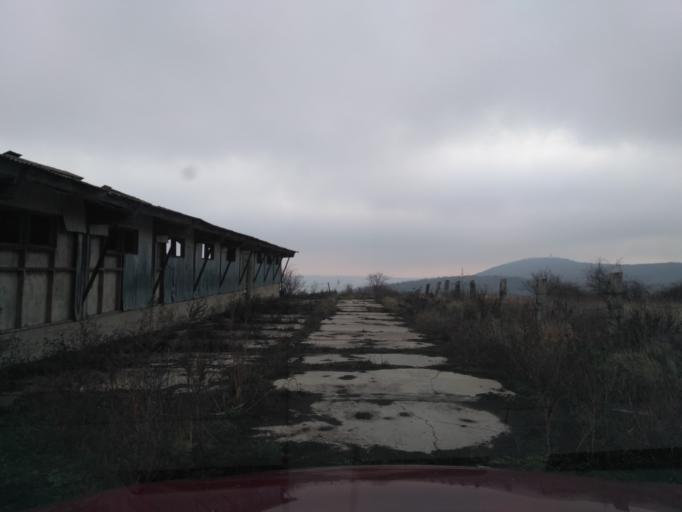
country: SK
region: Kosicky
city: Kosice
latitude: 48.7802
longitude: 21.2210
